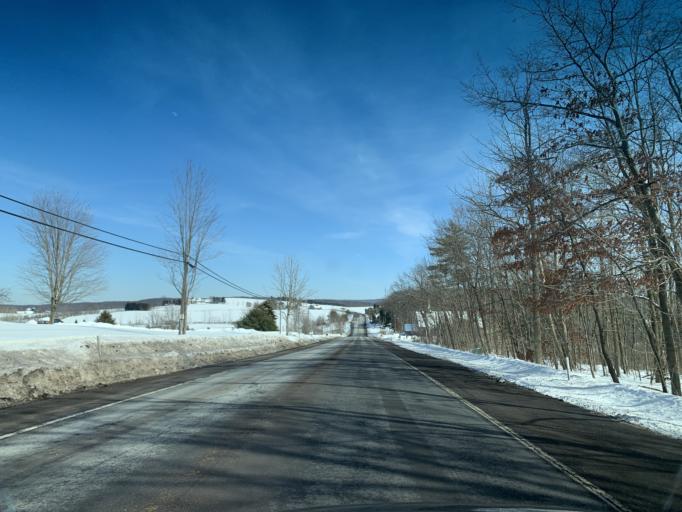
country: US
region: Maryland
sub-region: Allegany County
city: Frostburg
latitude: 39.6871
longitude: -79.0294
